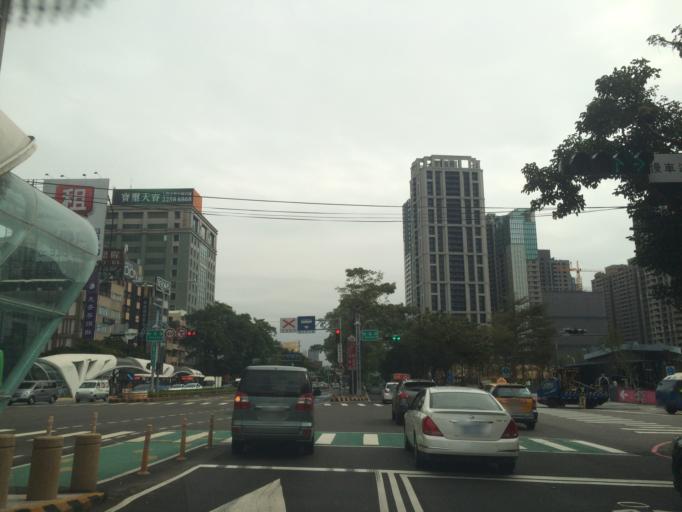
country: TW
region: Taiwan
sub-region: Taichung City
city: Taichung
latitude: 24.1691
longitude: 120.6389
